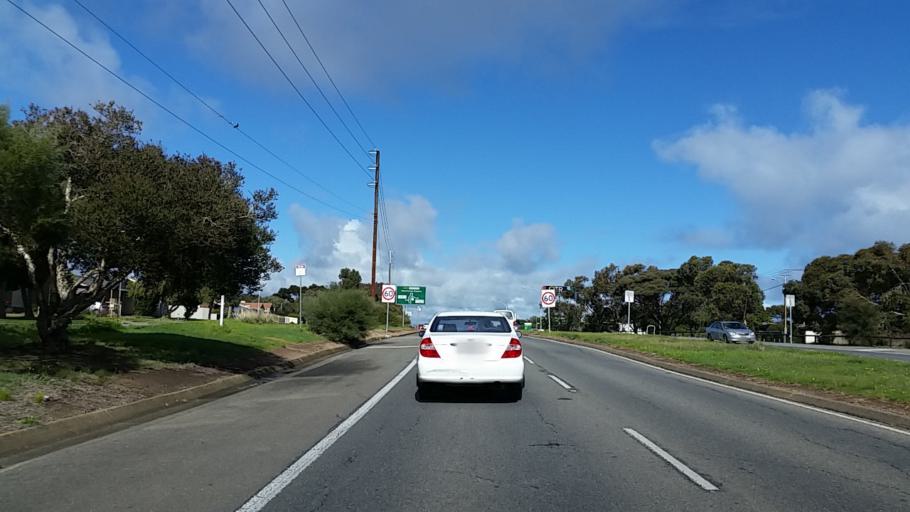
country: AU
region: South Australia
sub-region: Adelaide
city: Port Noarlunga
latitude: -35.1279
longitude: 138.4856
